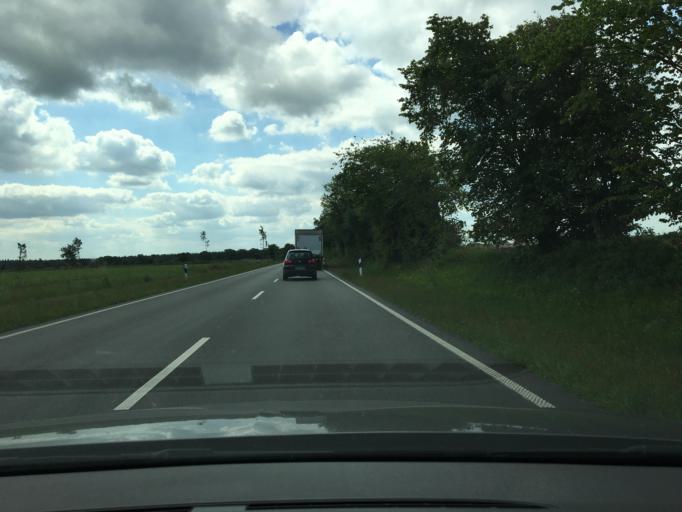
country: DE
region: Schleswig-Holstein
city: Klein Rheide
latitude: 54.4378
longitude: 9.4839
